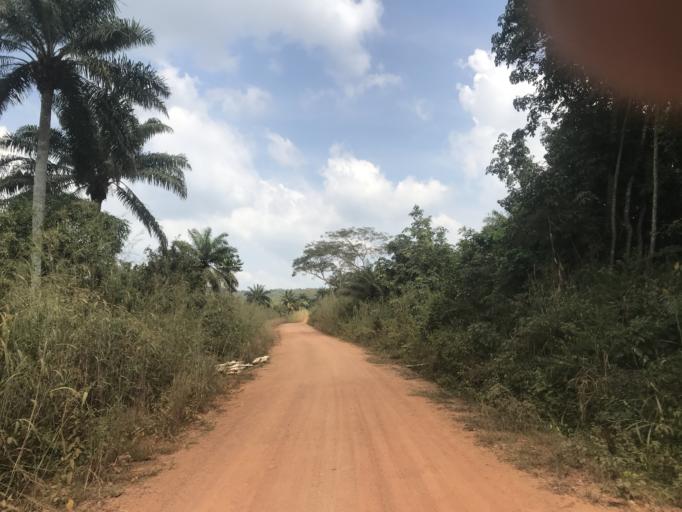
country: NG
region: Osun
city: Inisa
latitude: 7.8896
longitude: 4.3956
